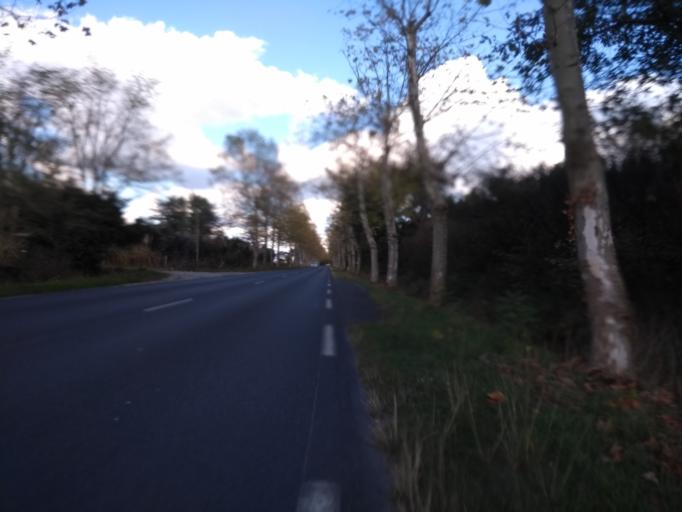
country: FR
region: Aquitaine
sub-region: Departement de la Gironde
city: Saint-Aubin-de-Medoc
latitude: 44.6926
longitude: -0.7138
